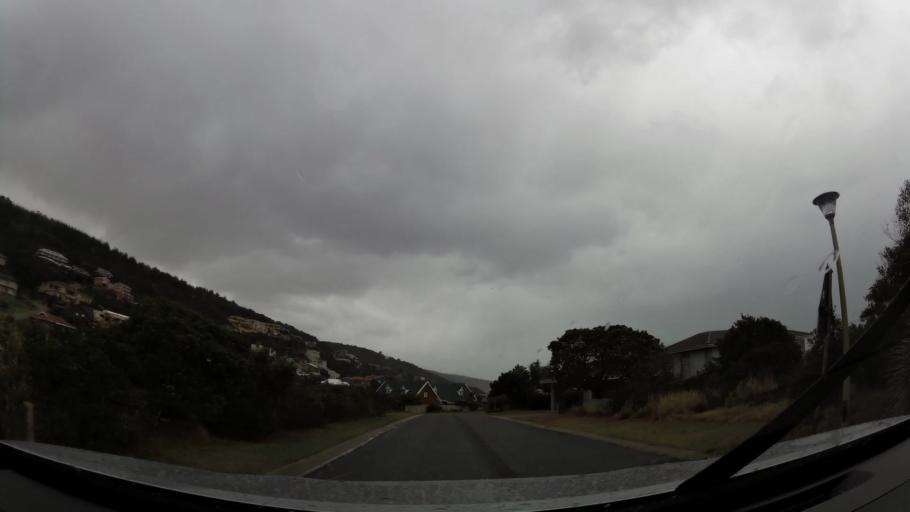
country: ZA
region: Western Cape
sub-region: Eden District Municipality
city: George
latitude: -34.0485
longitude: 22.2874
